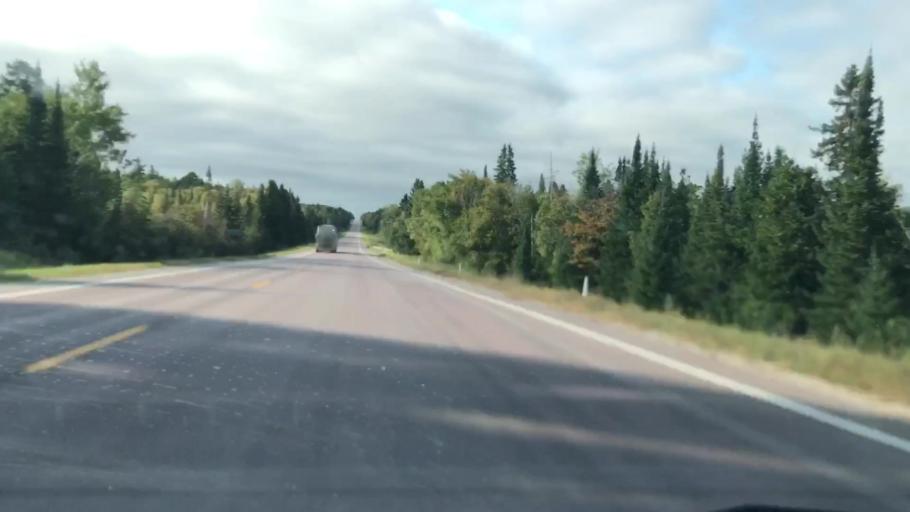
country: US
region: Michigan
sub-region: Luce County
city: Newberry
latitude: 46.3020
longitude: -85.5682
